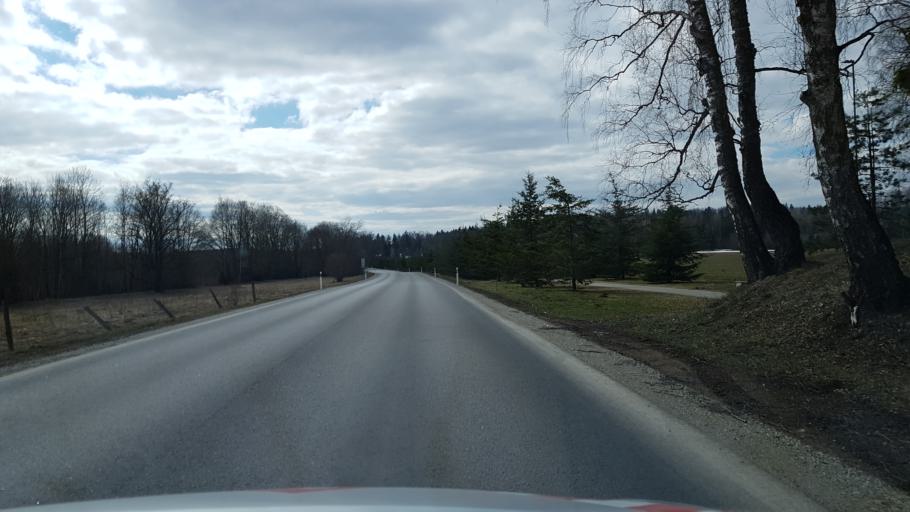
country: EE
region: Laeaene-Virumaa
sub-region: Vaeike-Maarja vald
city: Vaike-Maarja
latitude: 59.1091
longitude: 26.2353
